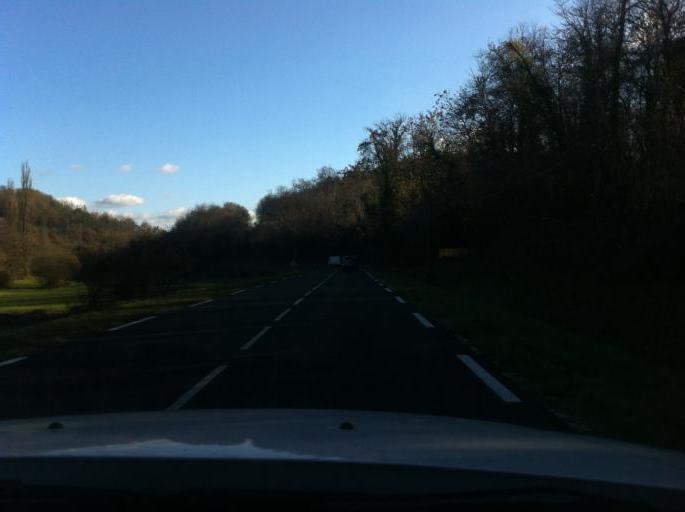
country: FR
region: Aquitaine
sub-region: Departement de la Dordogne
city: Rouffignac-Saint-Cernin-de-Reilhac
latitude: 45.0364
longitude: 0.8968
